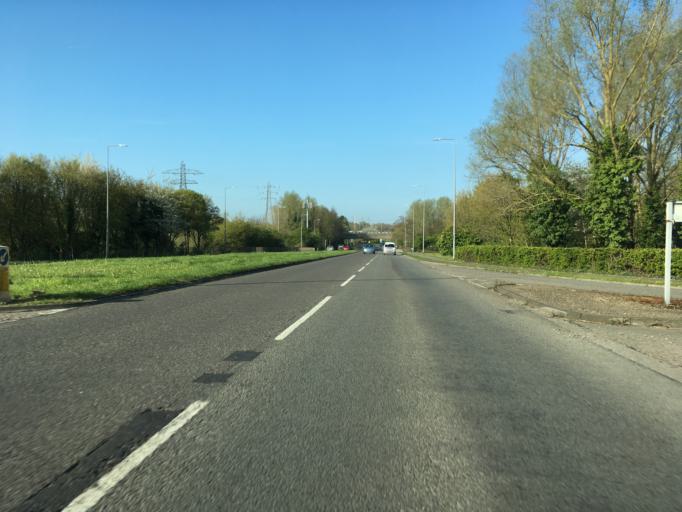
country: GB
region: England
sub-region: Milton Keynes
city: Bradwell
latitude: 52.0517
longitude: -0.7923
